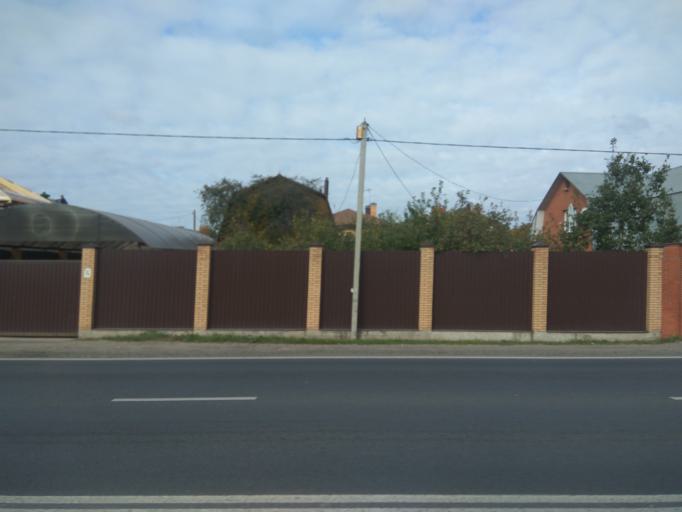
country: RU
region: Moskovskaya
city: Medvezh'i Ozera
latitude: 55.8673
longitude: 37.9916
